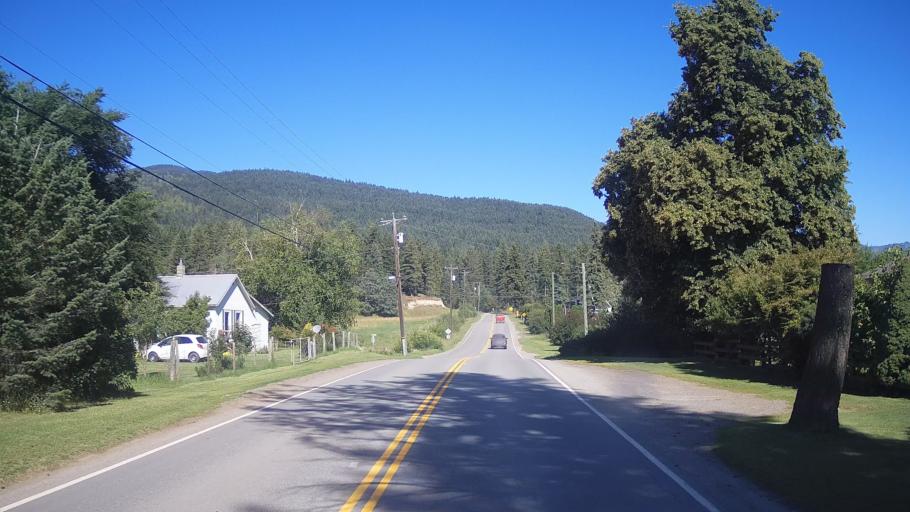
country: CA
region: British Columbia
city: Kamloops
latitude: 51.4250
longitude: -120.2077
